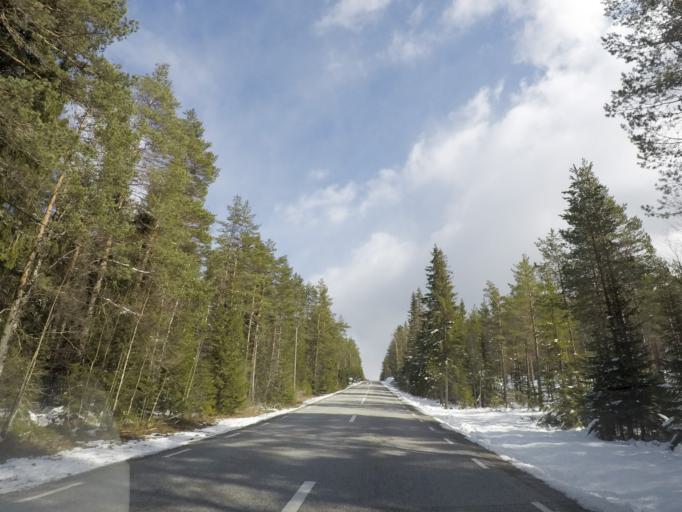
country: SE
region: OErebro
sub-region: Lindesbergs Kommun
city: Stora
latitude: 59.8991
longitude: 15.2186
